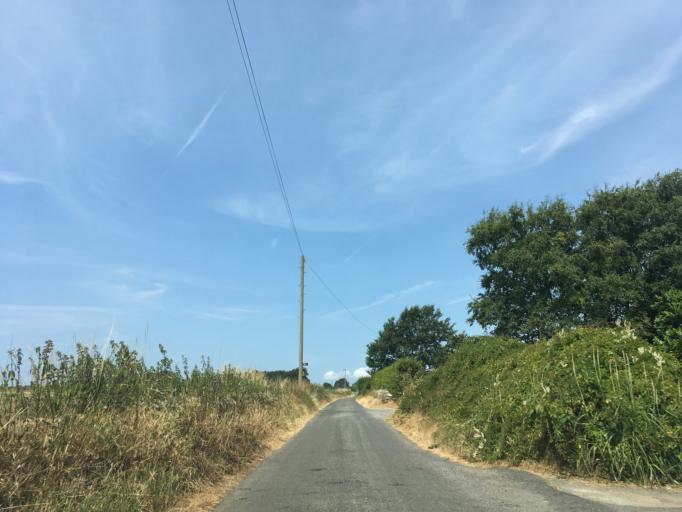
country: GB
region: England
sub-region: Gloucestershire
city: Nailsworth
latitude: 51.6679
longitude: -2.2742
